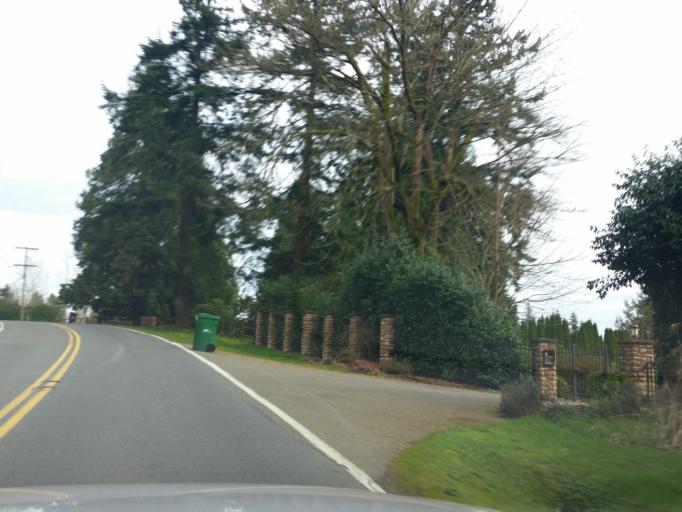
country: US
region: Washington
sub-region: King County
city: Woodinville
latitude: 47.7545
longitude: -122.1307
